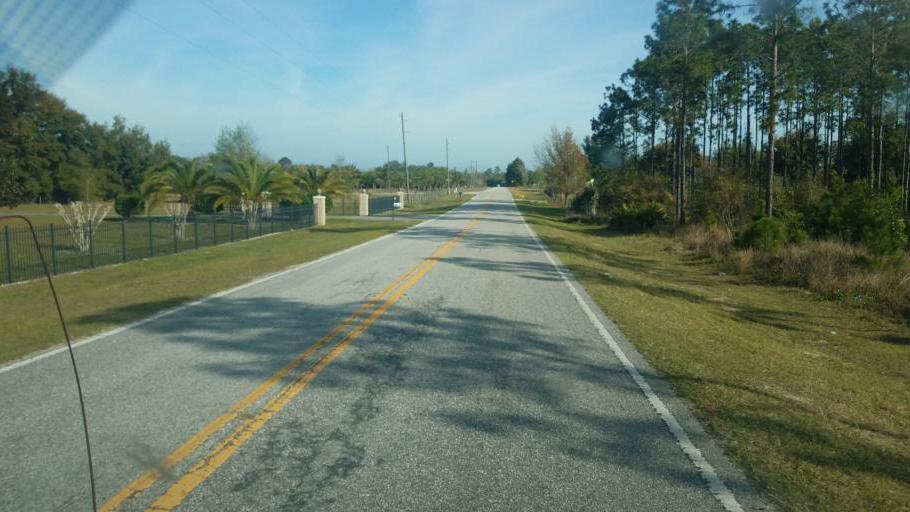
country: US
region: Florida
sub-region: Lake County
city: Clermont
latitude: 28.4525
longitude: -81.7962
